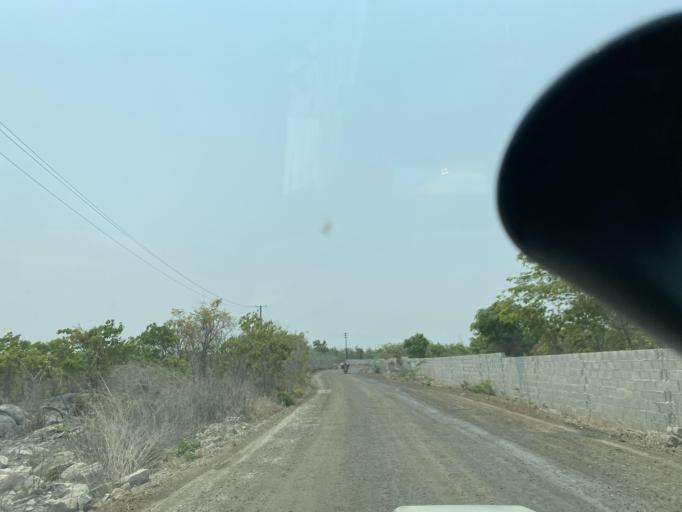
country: ZM
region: Lusaka
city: Lusaka
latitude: -15.5338
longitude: 28.4477
